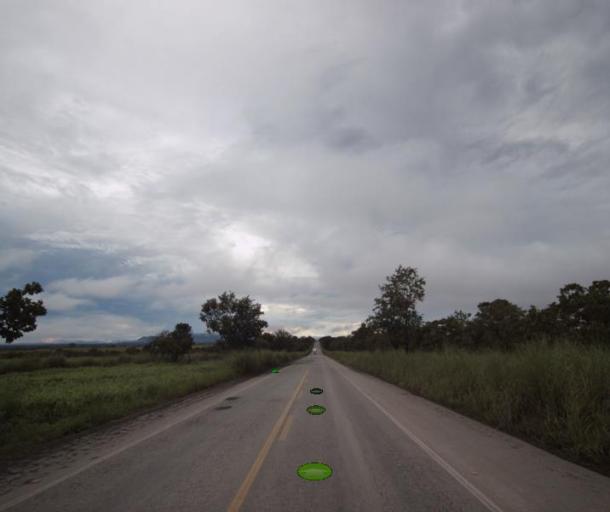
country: BR
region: Goias
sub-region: Porangatu
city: Porangatu
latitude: -13.5323
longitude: -49.1106
